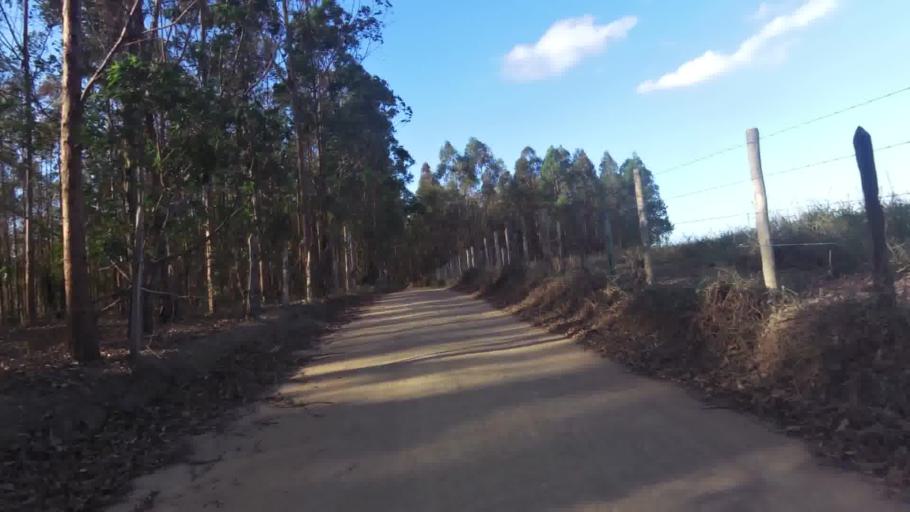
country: BR
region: Espirito Santo
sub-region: Marataizes
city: Marataizes
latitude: -21.1662
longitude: -41.0433
